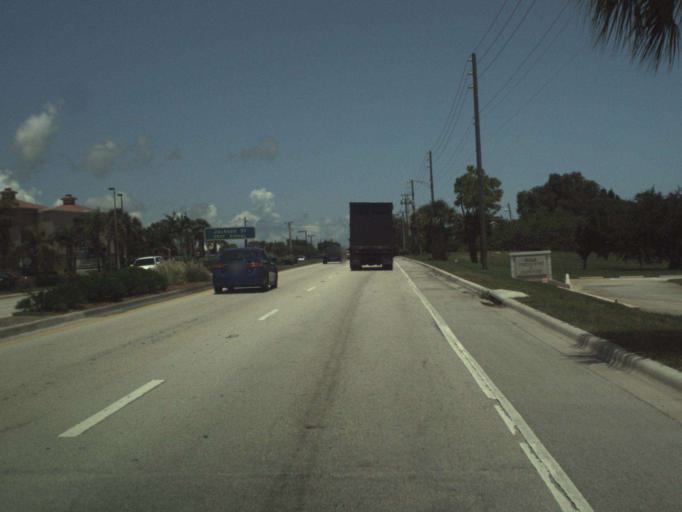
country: US
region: Florida
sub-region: Indian River County
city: Sebastian
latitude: 27.8245
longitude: -80.4747
